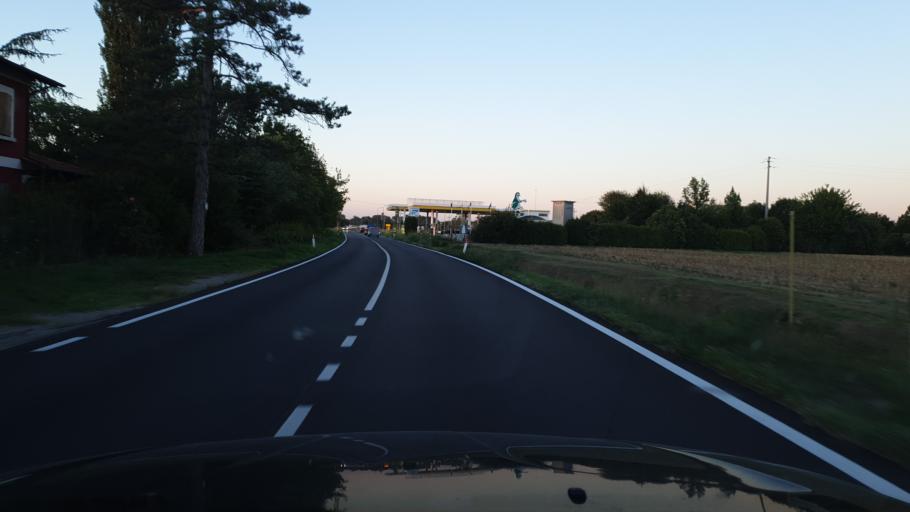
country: IT
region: Emilia-Romagna
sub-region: Provincia di Bologna
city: Granarolo dell'Emilia e Viadagola
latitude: 44.5878
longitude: 11.4300
